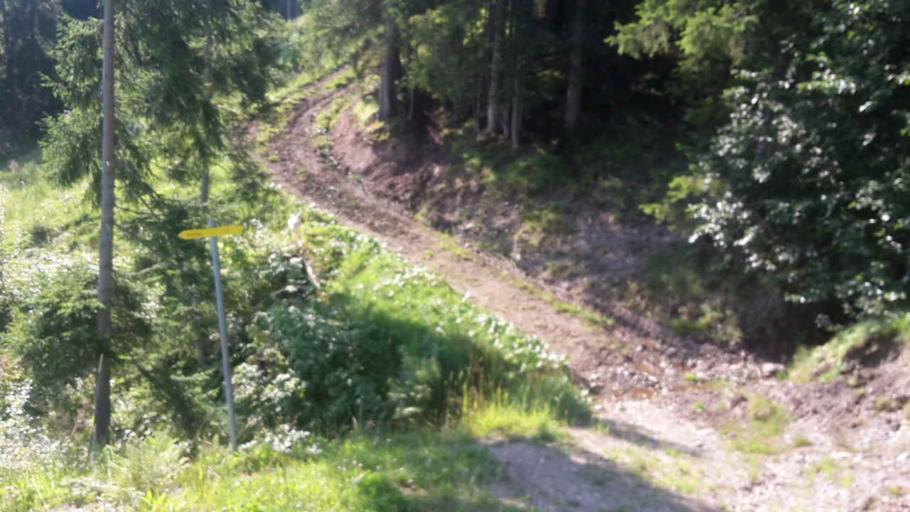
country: AT
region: Tyrol
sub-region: Politischer Bezirk Kitzbuhel
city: Kirchberg in Tirol
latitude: 47.4297
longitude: 12.3347
